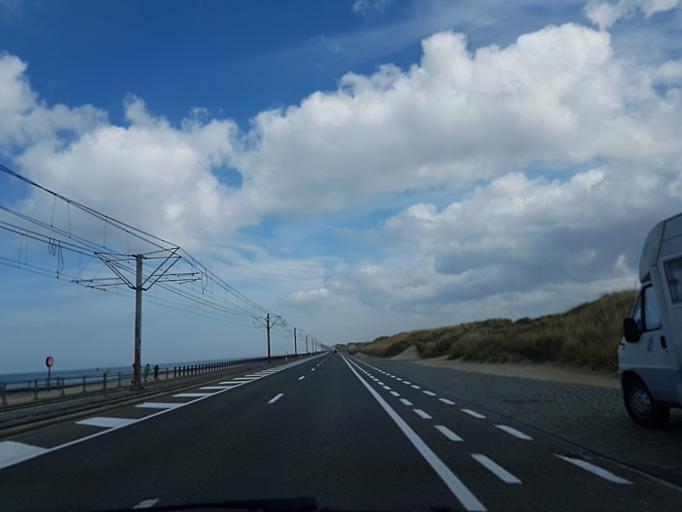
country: BE
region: Flanders
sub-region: Provincie West-Vlaanderen
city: Middelkerke
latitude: 51.1961
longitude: 2.8336
